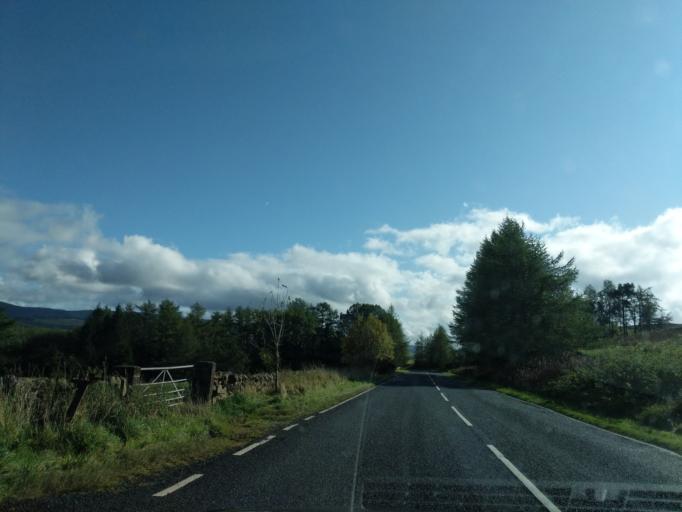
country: GB
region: Scotland
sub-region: Dumfries and Galloway
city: Moffat
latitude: 55.3572
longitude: -3.4717
